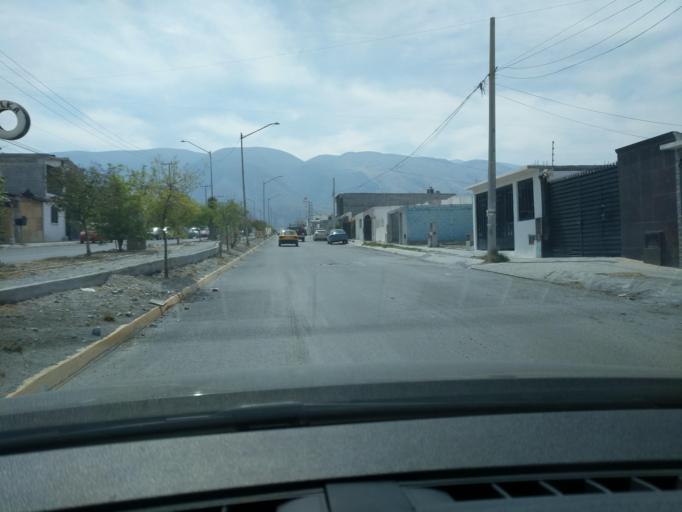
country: MX
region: Coahuila
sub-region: Arteaga
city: Arteaga
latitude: 25.4223
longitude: -100.9017
